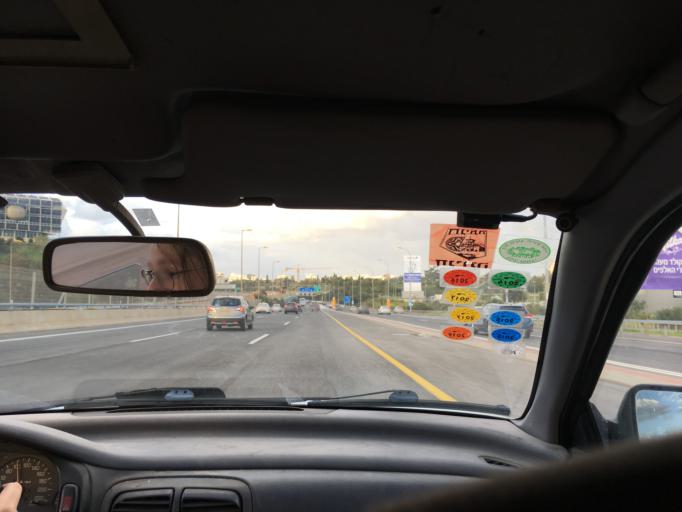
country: IL
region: Tel Aviv
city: Ramat Gan
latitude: 32.1076
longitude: 34.8075
